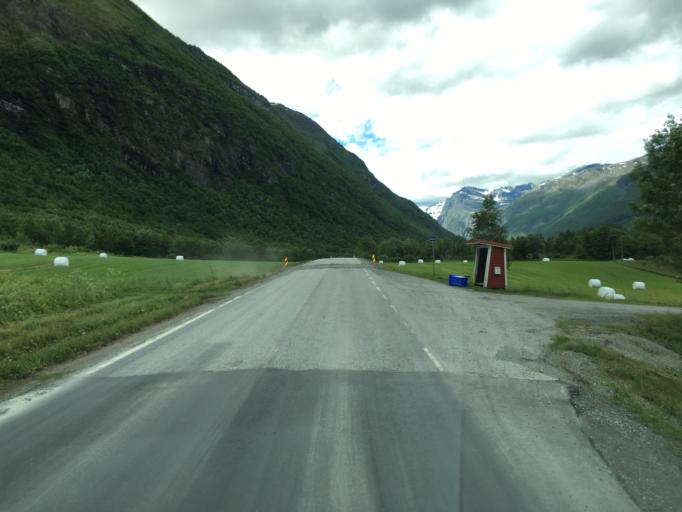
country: NO
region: More og Romsdal
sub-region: Sunndal
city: Sunndalsora
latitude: 62.5948
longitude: 8.9573
